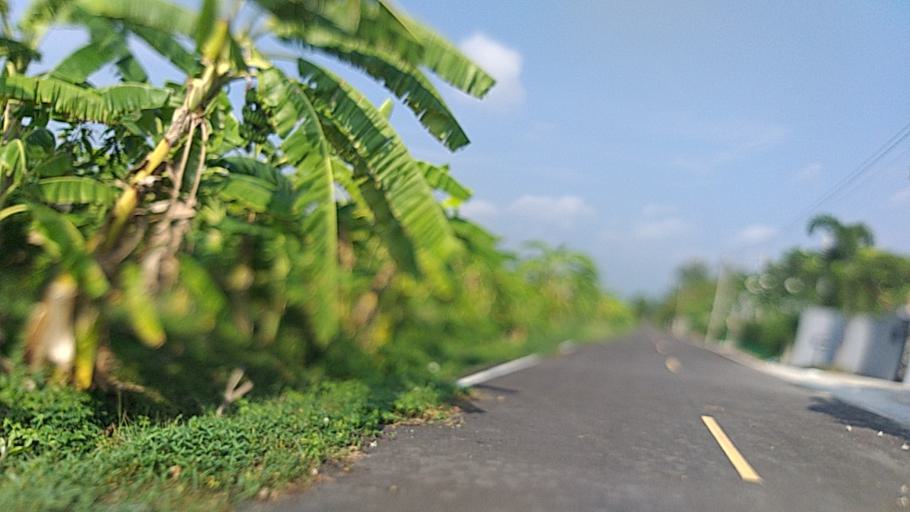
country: TH
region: Pathum Thani
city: Nong Suea
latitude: 14.1013
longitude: 100.8652
